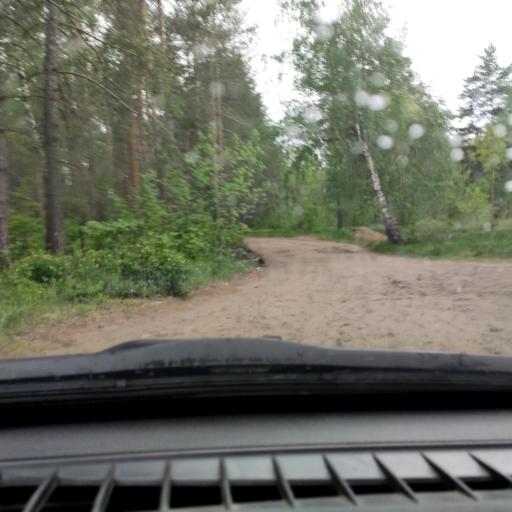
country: RU
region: Samara
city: Zhigulevsk
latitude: 53.5305
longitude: 49.5551
